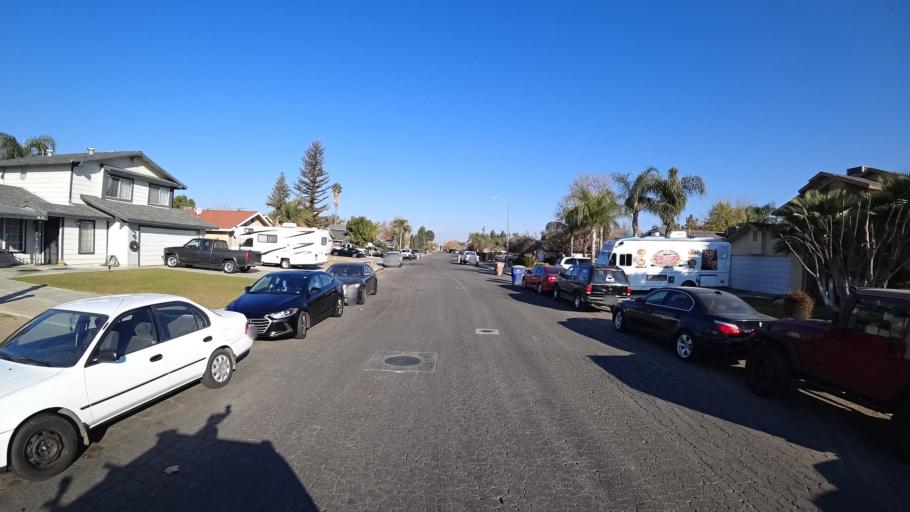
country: US
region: California
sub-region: Kern County
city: Greenfield
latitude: 35.3017
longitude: -119.0147
